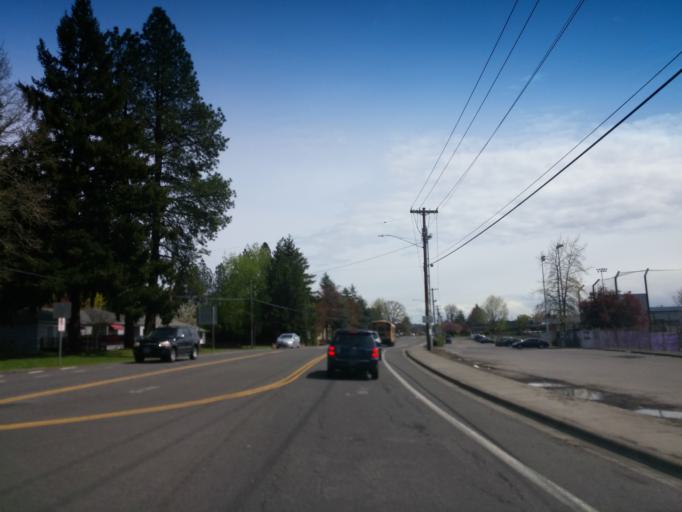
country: US
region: Oregon
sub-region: Washington County
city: Cedar Mill
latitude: 45.5304
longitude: -122.8229
